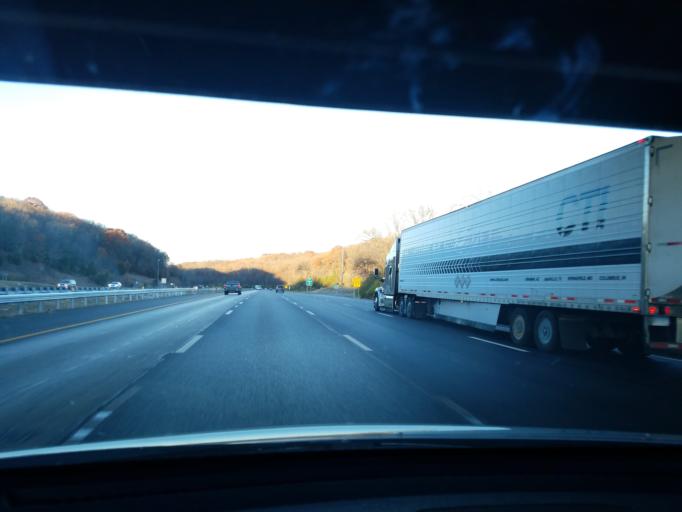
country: US
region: Missouri
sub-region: Jefferson County
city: High Ridge
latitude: 38.5152
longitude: -90.5498
